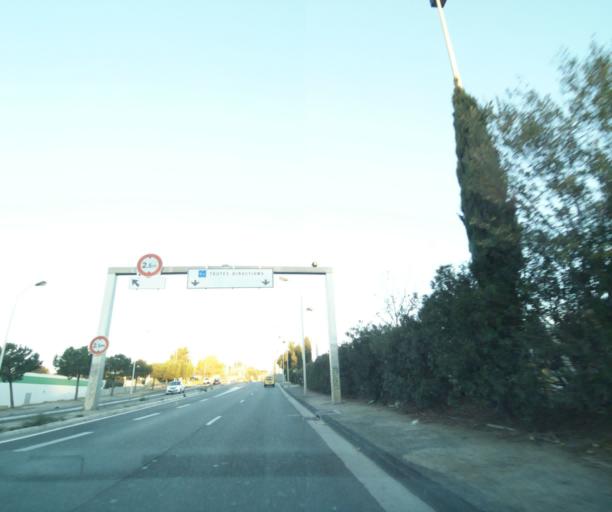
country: FR
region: Provence-Alpes-Cote d'Azur
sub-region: Departement des Bouches-du-Rhone
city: La Penne-sur-Huveaune
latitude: 43.2933
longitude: 5.4840
